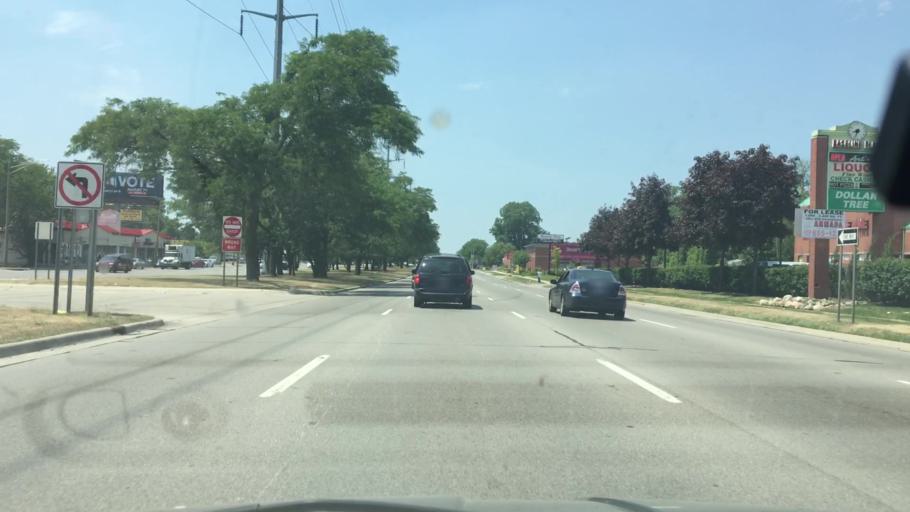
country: US
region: Michigan
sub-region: Oakland County
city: Southfield
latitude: 42.4440
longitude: -83.2420
